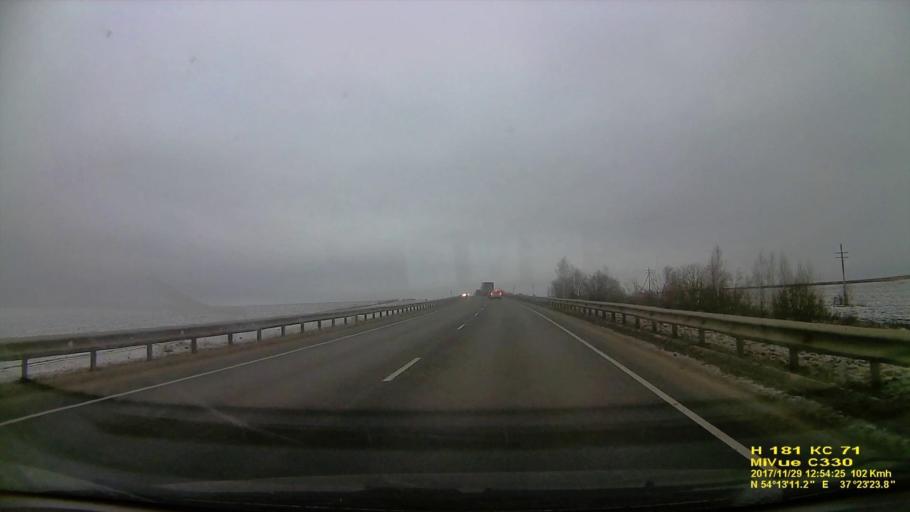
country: RU
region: Tula
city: Leninskiy
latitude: 54.2198
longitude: 37.3899
